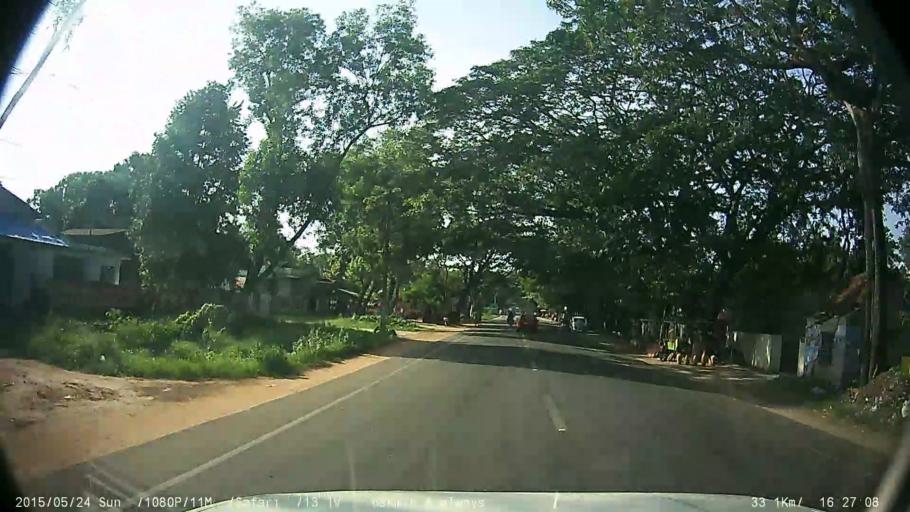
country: IN
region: Kerala
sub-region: Alappuzha
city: Alleppey
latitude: 9.5257
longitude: 76.3275
